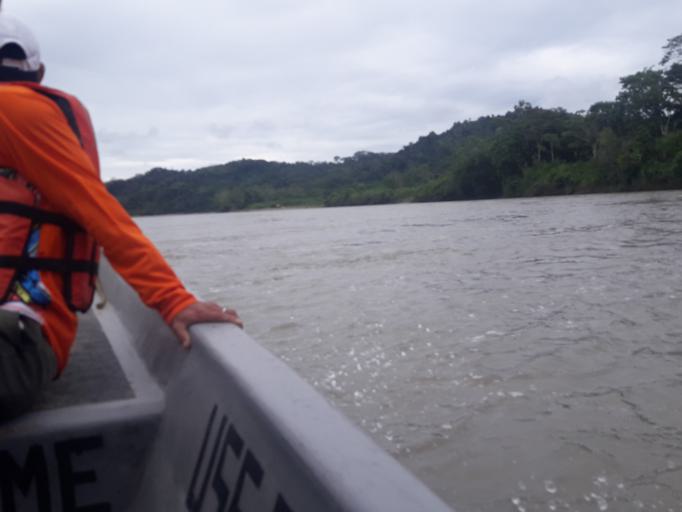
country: EC
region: Orellana
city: Boca Suno
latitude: -0.8809
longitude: -77.2831
